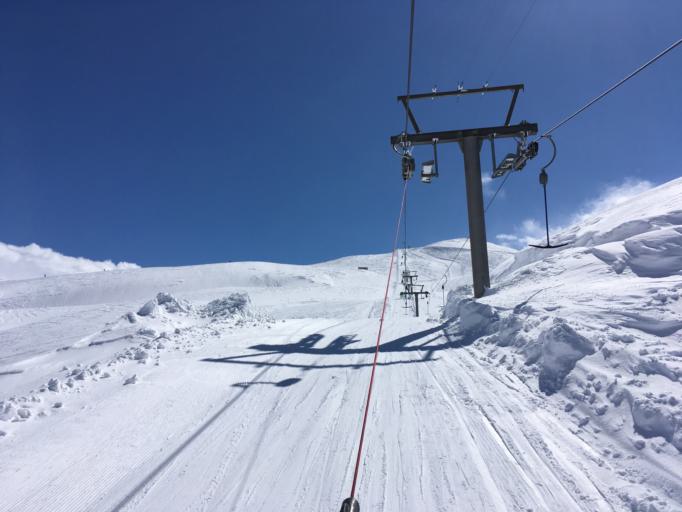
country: CH
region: Grisons
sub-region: Maloja District
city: Promontogno
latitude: 46.4402
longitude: 9.6364
